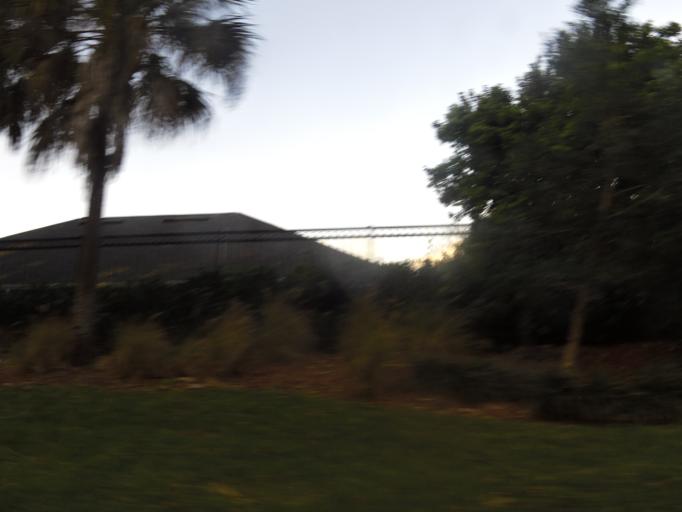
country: US
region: Florida
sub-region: Duval County
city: Jacksonville Beach
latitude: 30.2660
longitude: -81.4639
